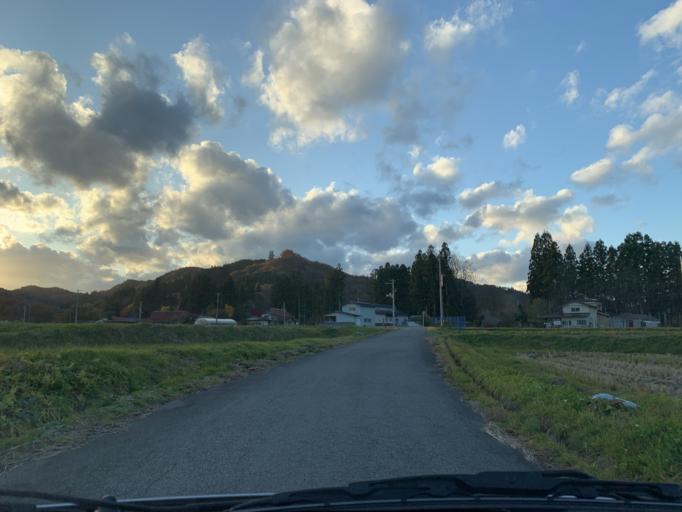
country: JP
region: Iwate
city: Mizusawa
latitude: 39.0440
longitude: 141.0500
